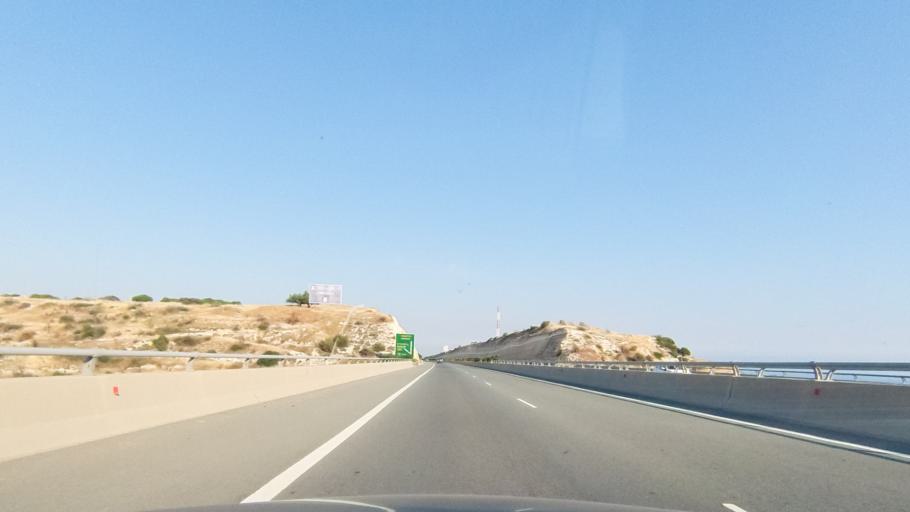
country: CY
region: Limassol
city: Sotira
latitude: 34.6877
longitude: 32.8743
